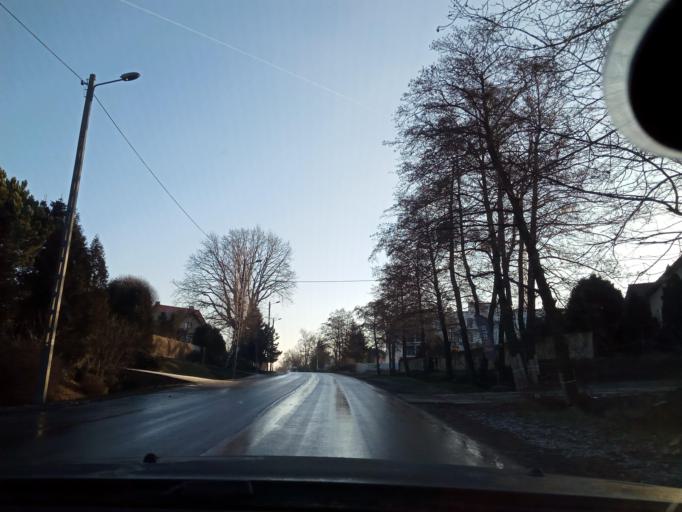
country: PL
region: Lesser Poland Voivodeship
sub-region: Powiat wielicki
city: Kokotow
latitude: 50.1043
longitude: 20.0581
